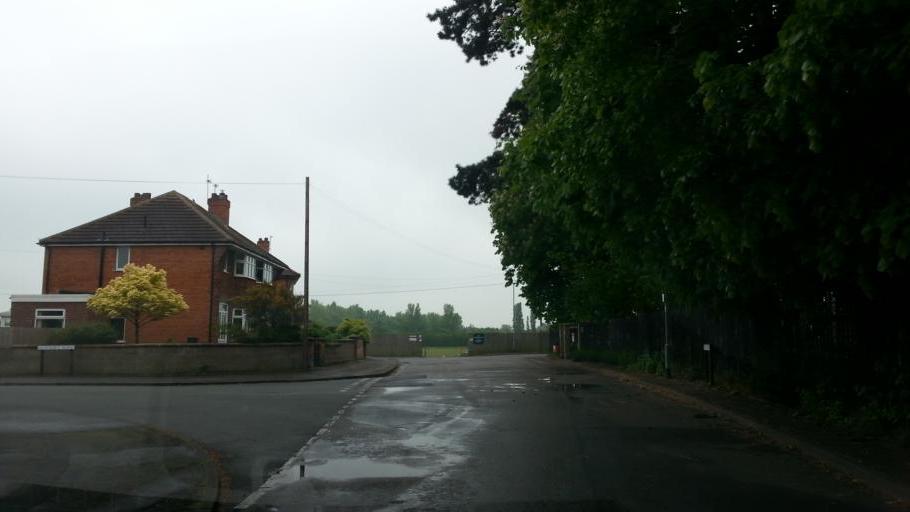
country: GB
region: England
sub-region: Nottinghamshire
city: Newark on Trent
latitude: 53.0645
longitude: -0.7986
